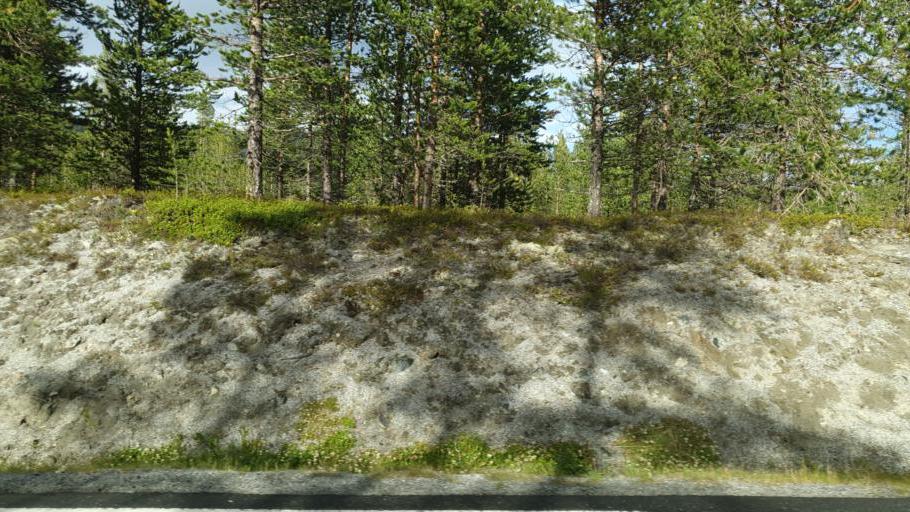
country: NO
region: Oppland
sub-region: Vaga
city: Vagamo
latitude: 61.8199
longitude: 8.9805
